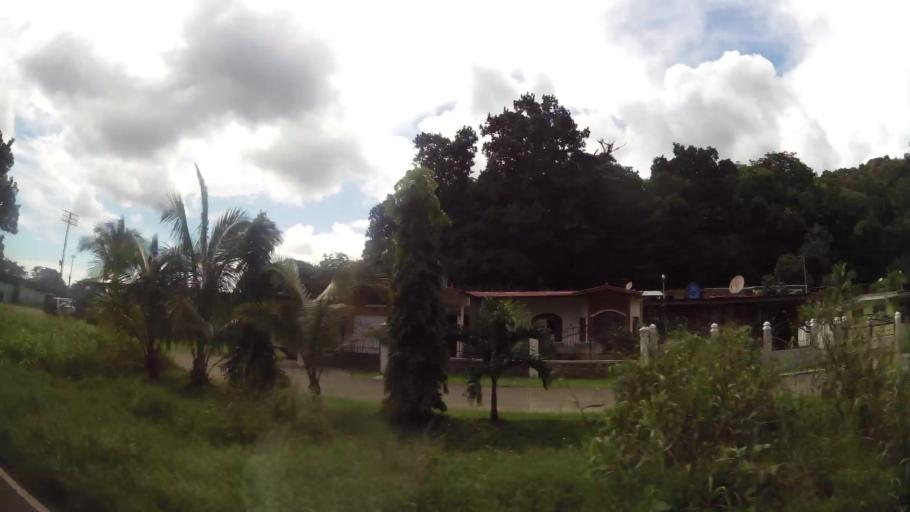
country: PA
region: Panama
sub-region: Distrito de Panama
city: Paraiso
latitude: 9.0286
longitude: -79.6222
